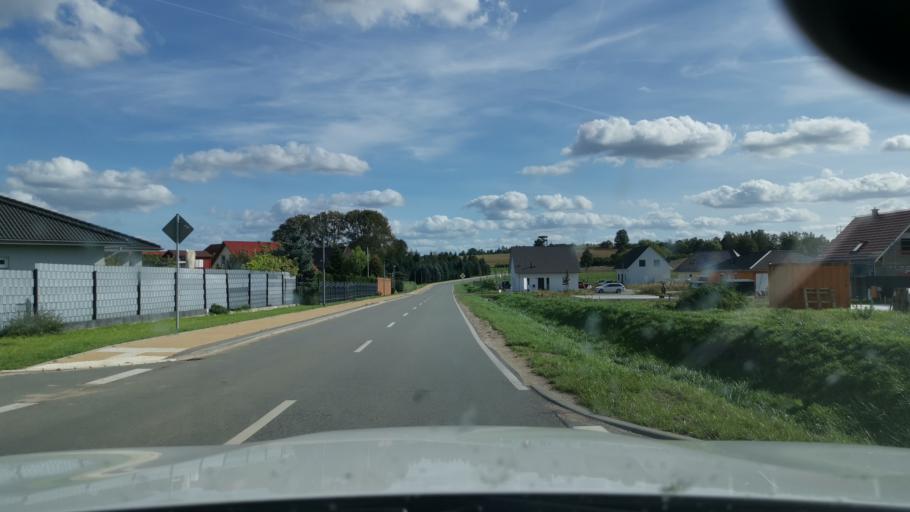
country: DE
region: Mecklenburg-Vorpommern
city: Tessin
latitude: 54.0280
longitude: 12.4500
